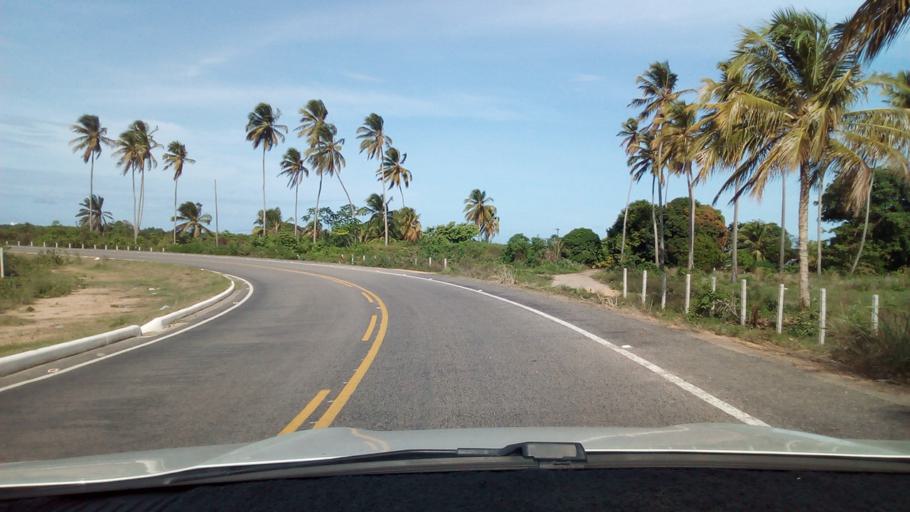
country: BR
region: Paraiba
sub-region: Cabedelo
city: Cabedelo
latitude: -6.9956
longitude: -34.8747
